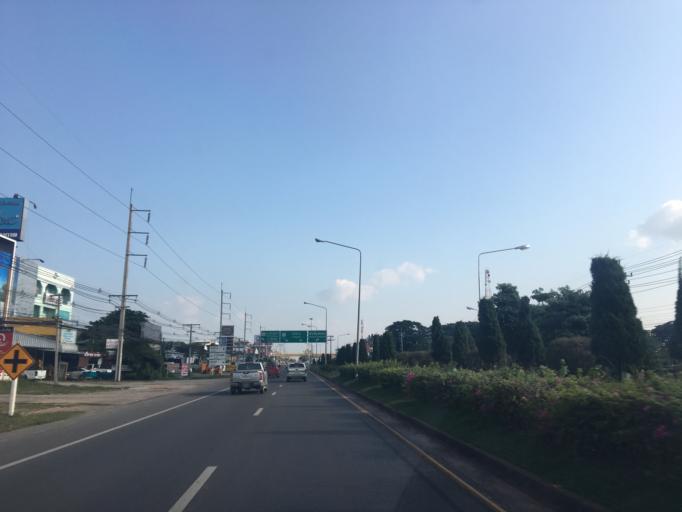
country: TH
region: Phayao
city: Phayao
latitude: 19.1745
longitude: 99.9039
